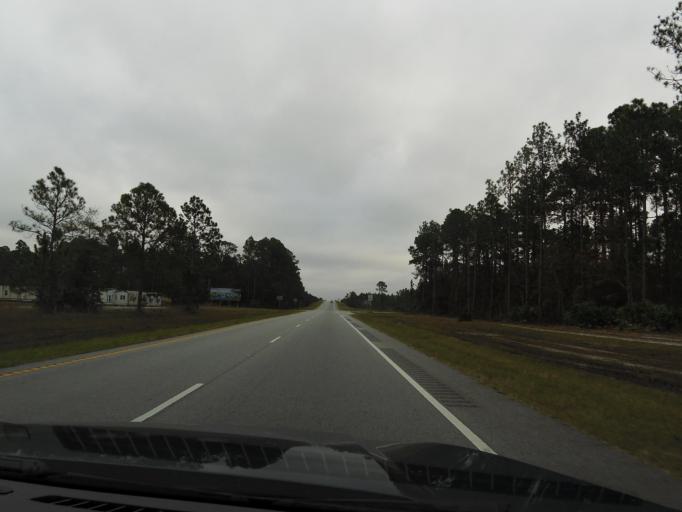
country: US
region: Georgia
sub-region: Charlton County
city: Folkston
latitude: 30.8714
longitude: -82.0227
